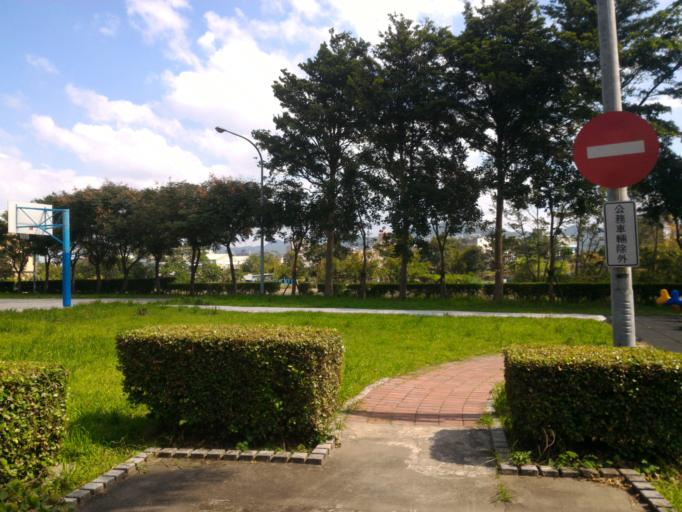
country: TW
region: Taipei
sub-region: Taipei
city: Banqiao
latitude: 24.9614
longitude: 121.4001
